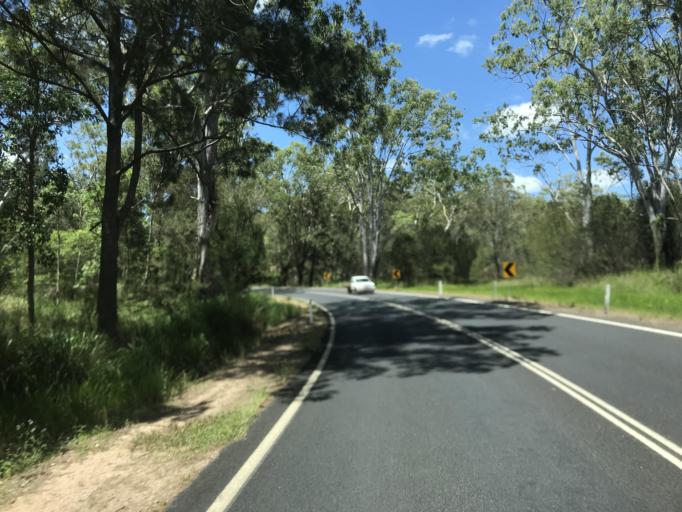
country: AU
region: Queensland
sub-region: Tablelands
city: Atherton
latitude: -17.4033
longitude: 145.3900
